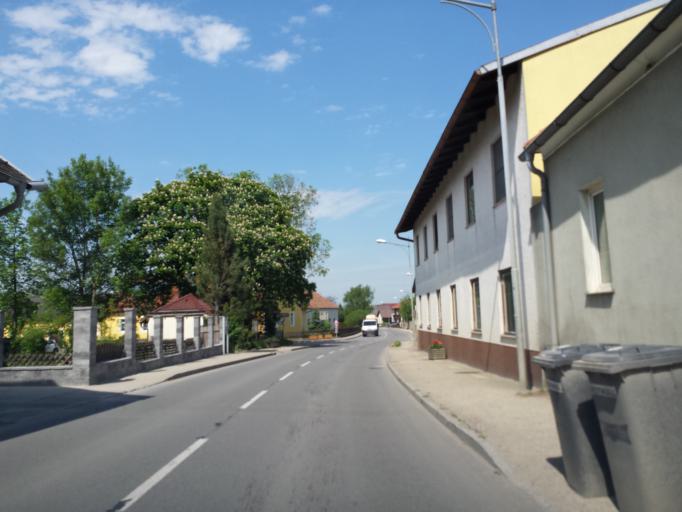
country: AT
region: Lower Austria
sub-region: Politischer Bezirk Tulln
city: Atzenbrugg
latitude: 48.3043
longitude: 15.8979
